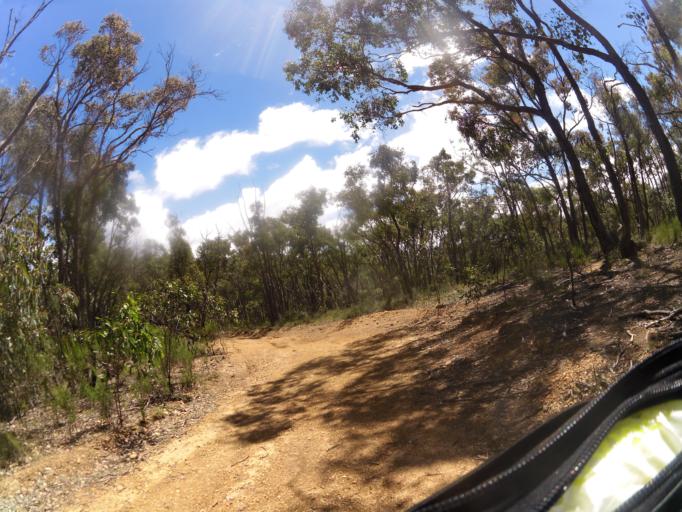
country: AU
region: Victoria
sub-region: Mount Alexander
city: Castlemaine
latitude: -37.0653
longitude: 144.2661
